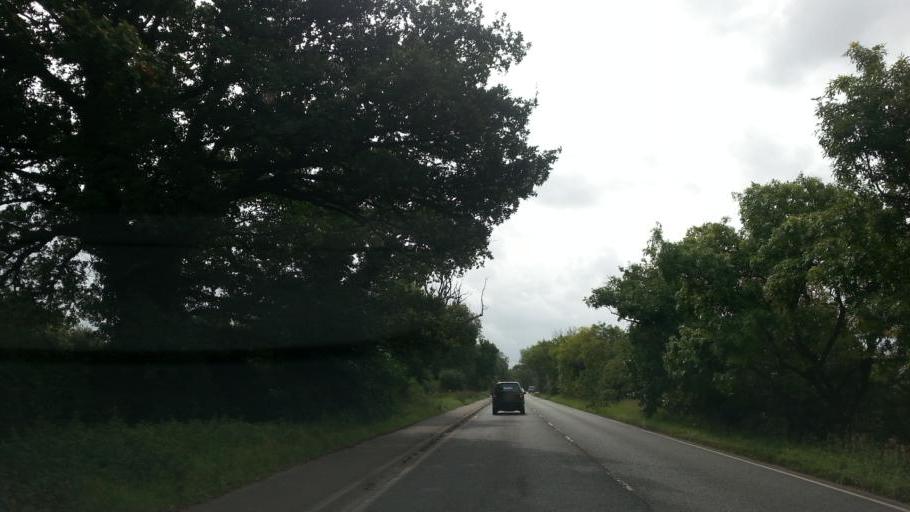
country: GB
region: England
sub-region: Cambridgeshire
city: Waterbeach
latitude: 52.2577
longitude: 0.1768
